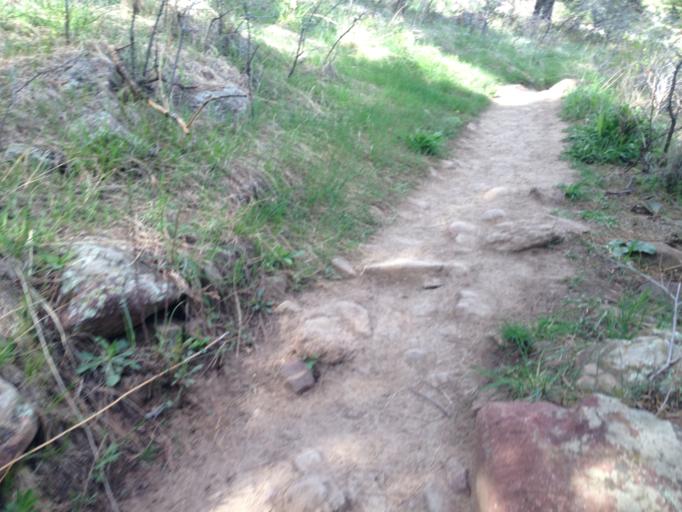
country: US
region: Colorado
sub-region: Boulder County
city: Boulder
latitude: 39.9439
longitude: -105.2761
